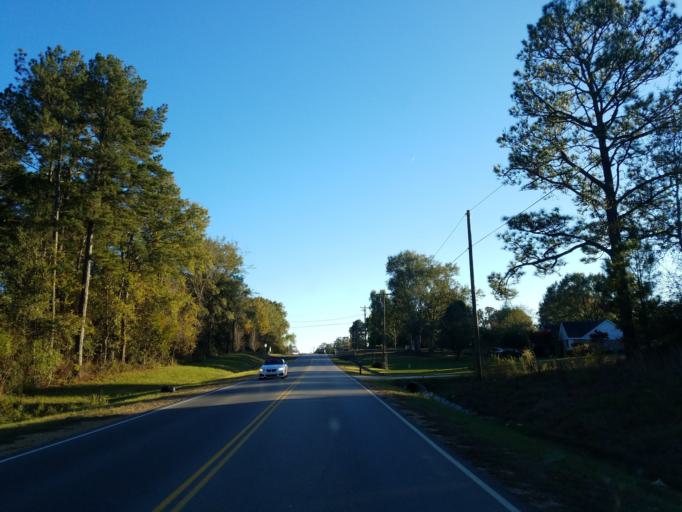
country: US
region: Mississippi
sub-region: Lamar County
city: Arnold Line
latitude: 31.3433
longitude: -89.3990
